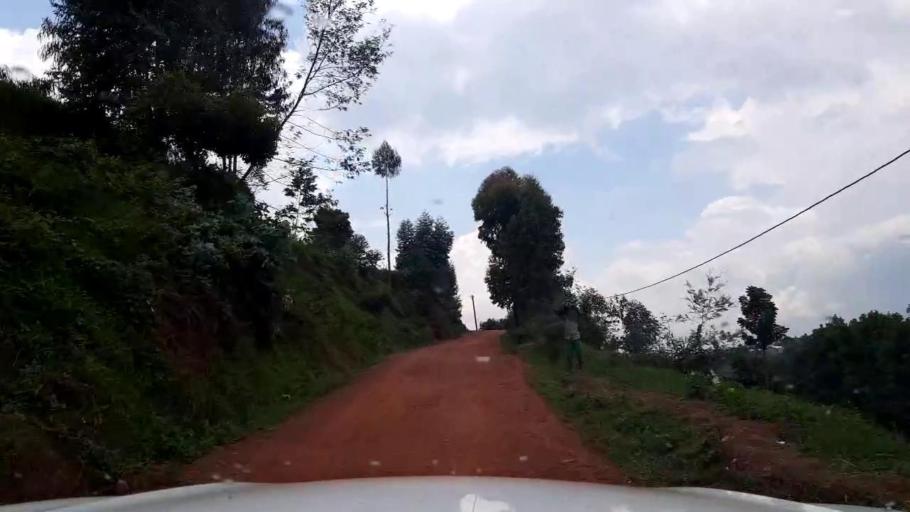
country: RW
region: Northern Province
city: Byumba
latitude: -1.5272
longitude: 29.9582
